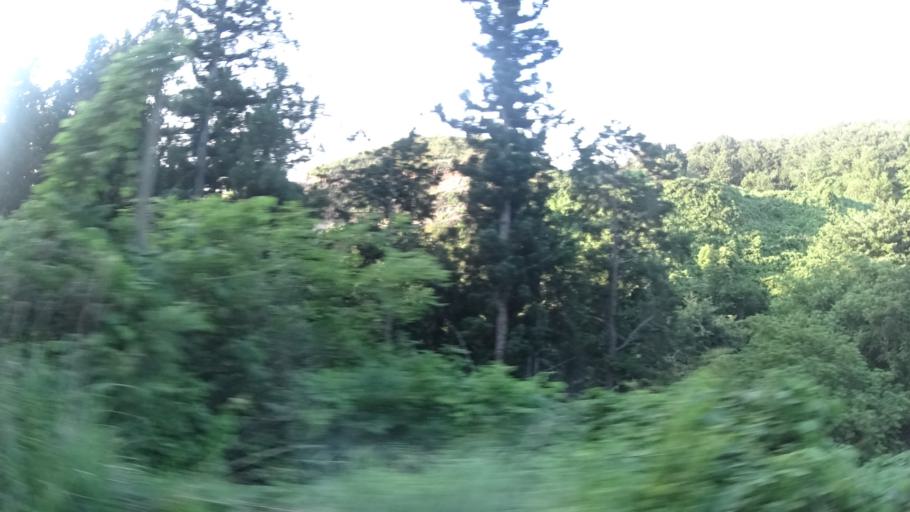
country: JP
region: Fukushima
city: Miharu
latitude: 37.4559
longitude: 140.5034
